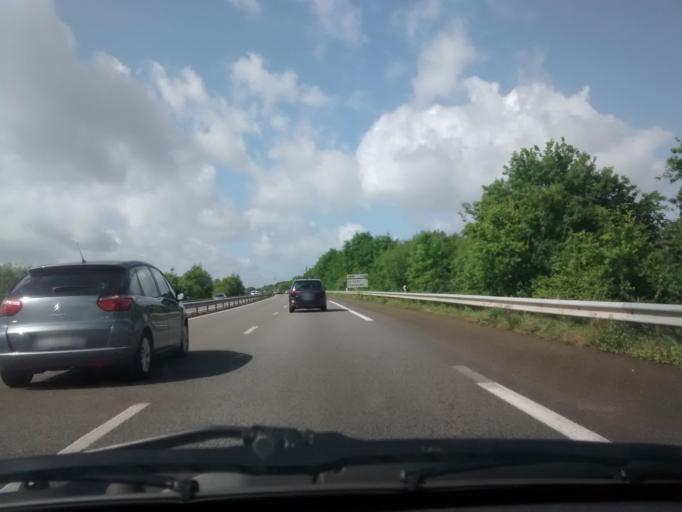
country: FR
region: Brittany
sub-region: Departement d'Ille-et-Vilaine
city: Le Rheu
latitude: 48.0886
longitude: -1.7801
